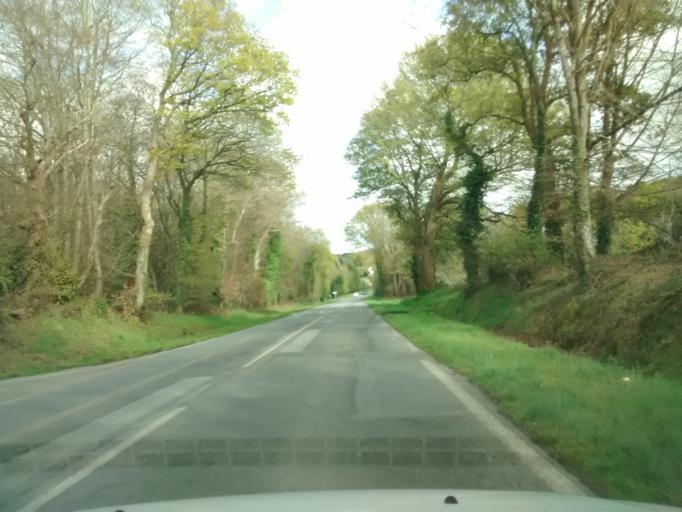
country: FR
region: Brittany
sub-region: Departement du Morbihan
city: Queven
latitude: 47.7787
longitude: -3.4297
